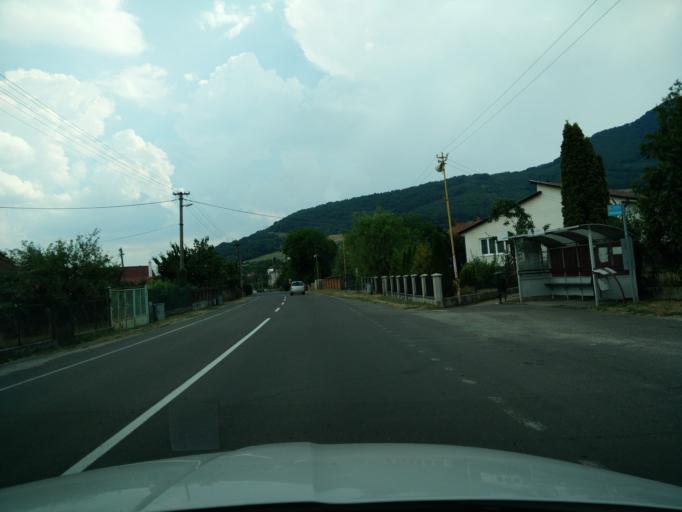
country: SK
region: Nitriansky
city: Novaky
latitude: 48.7948
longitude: 18.4773
